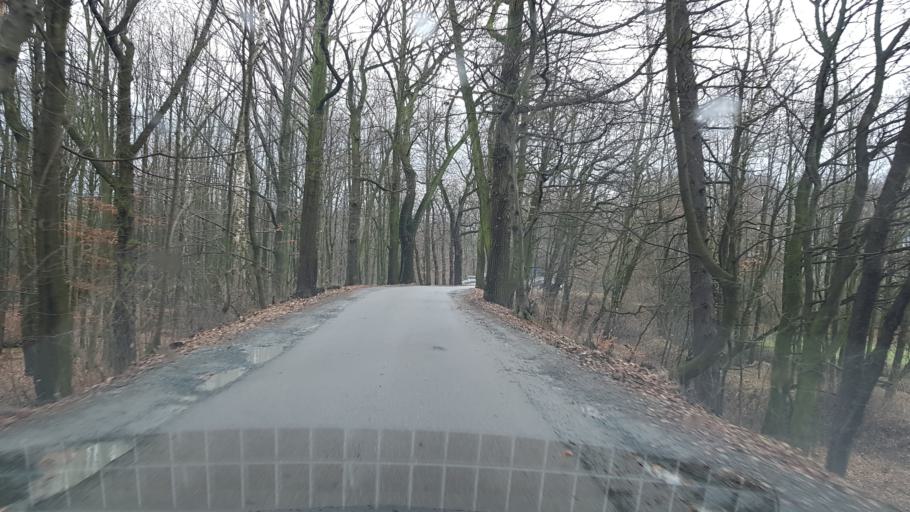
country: PL
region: Silesian Voivodeship
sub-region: Powiat pszczynski
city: Radostowice
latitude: 49.9744
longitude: 18.9049
